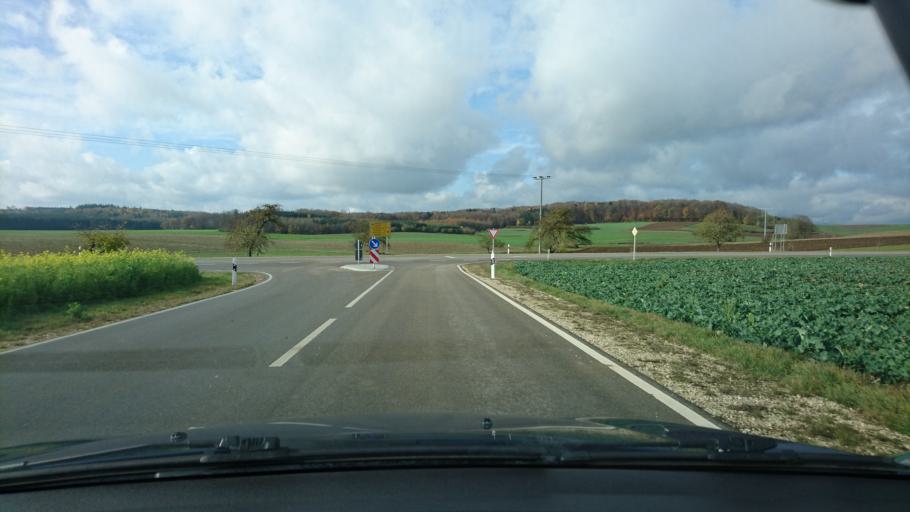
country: DE
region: Bavaria
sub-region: Swabia
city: Amerdingen
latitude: 48.7426
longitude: 10.4663
